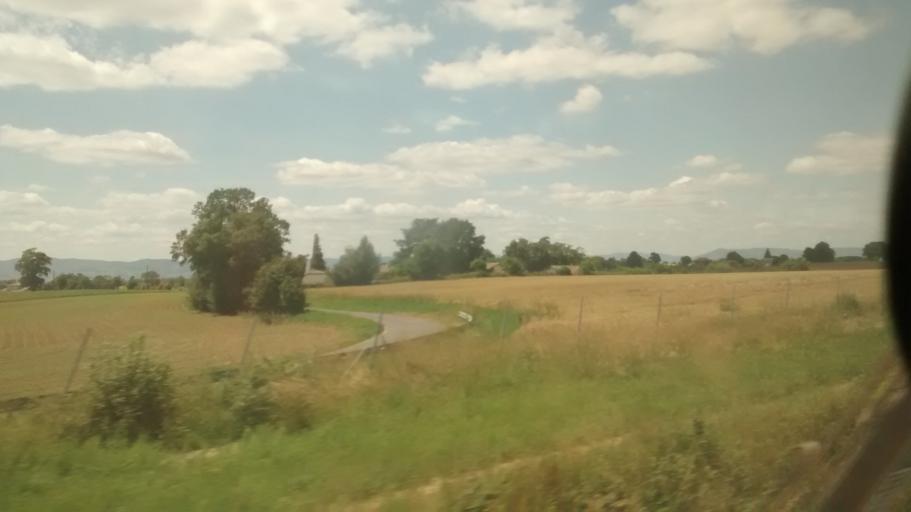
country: FR
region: Rhone-Alpes
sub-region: Departement de l'Ain
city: Villeneuve
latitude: 46.0031
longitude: 4.8579
